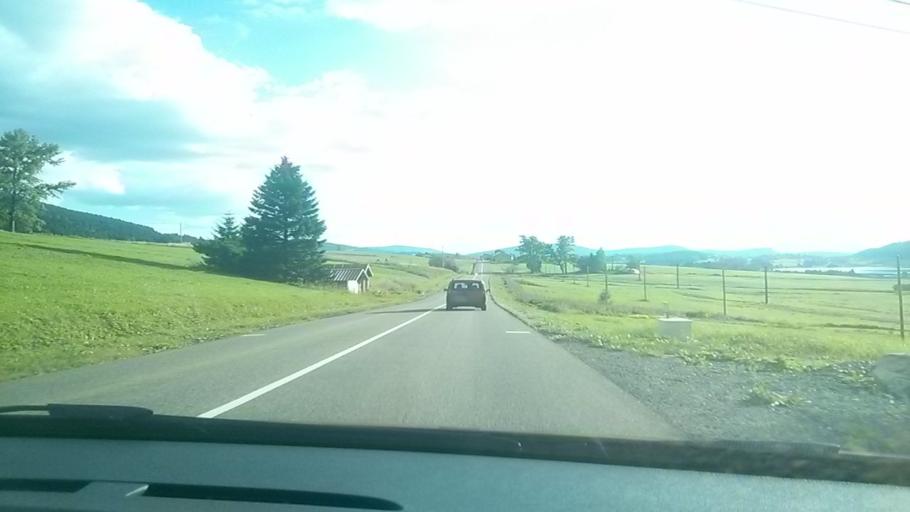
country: FR
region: Franche-Comte
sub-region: Departement du Jura
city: Les Rousses
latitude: 46.5100
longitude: 6.1099
